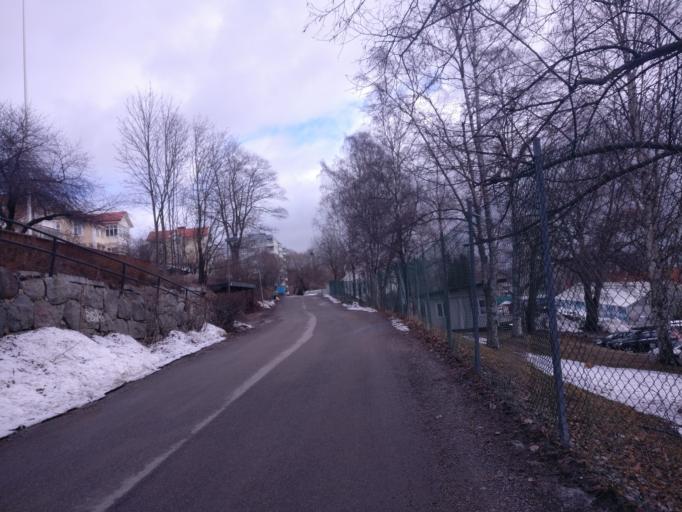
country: SE
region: Vaesternorrland
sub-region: Sundsvalls Kommun
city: Sundsvall
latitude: 62.3950
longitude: 17.3004
